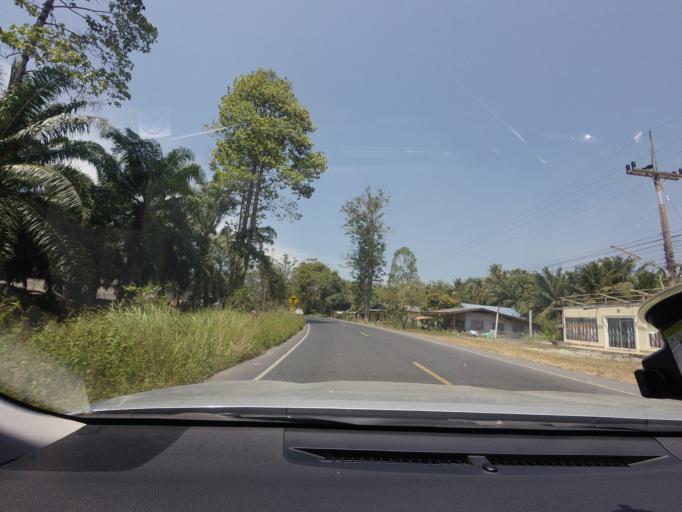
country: TH
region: Surat Thani
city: Tha Chang
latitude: 9.2668
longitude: 99.1562
